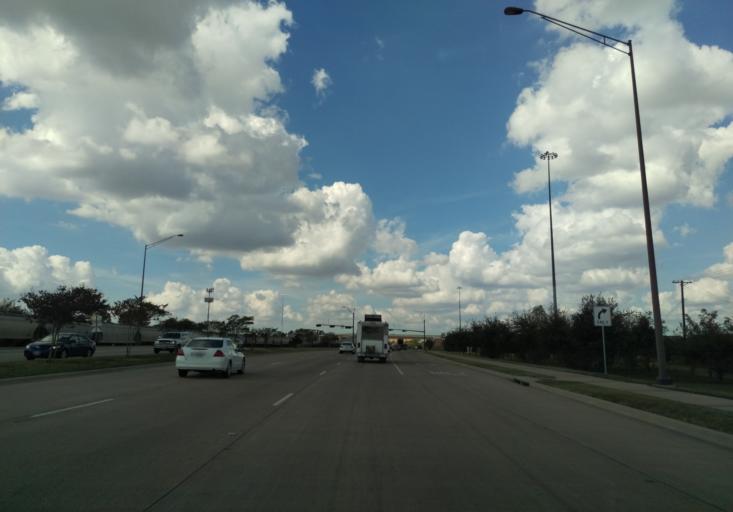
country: US
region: Texas
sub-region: Brazos County
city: College Station
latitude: 30.5838
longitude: -96.3250
